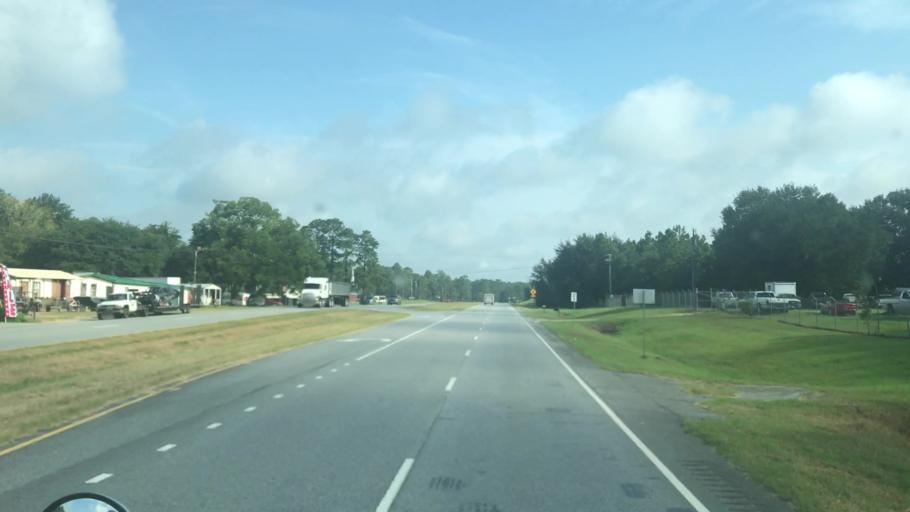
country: US
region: Georgia
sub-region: Decatur County
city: Bainbridge
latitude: 30.9434
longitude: -84.6102
